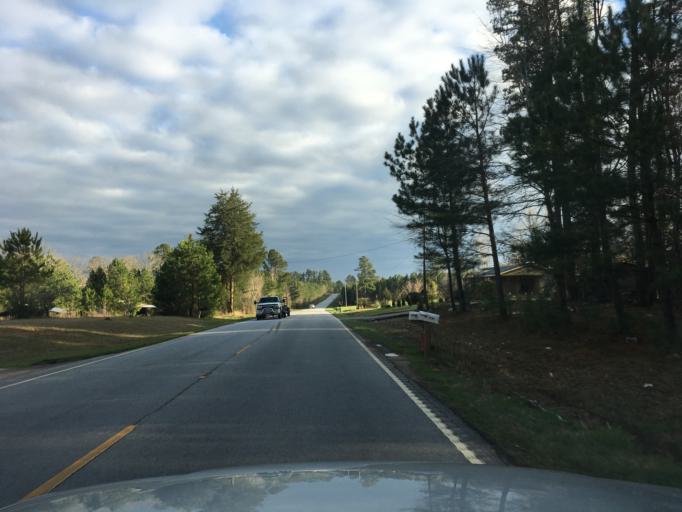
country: US
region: South Carolina
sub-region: Saluda County
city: Saluda
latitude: 34.0784
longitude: -81.8214
